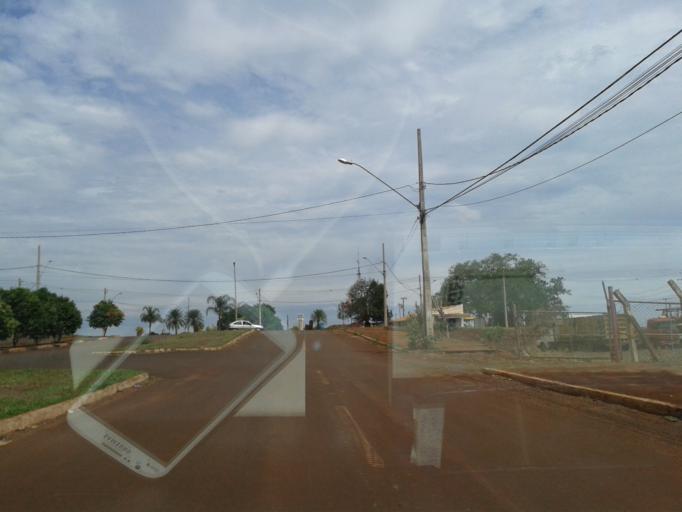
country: BR
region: Goias
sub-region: Itumbiara
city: Itumbiara
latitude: -18.4273
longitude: -49.1916
